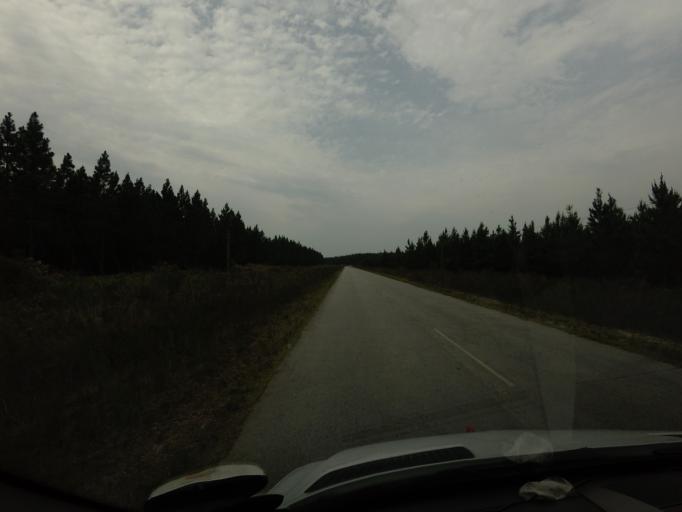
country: ZA
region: Eastern Cape
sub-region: Cacadu District Municipality
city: Kareedouw
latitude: -33.9784
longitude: 23.8403
